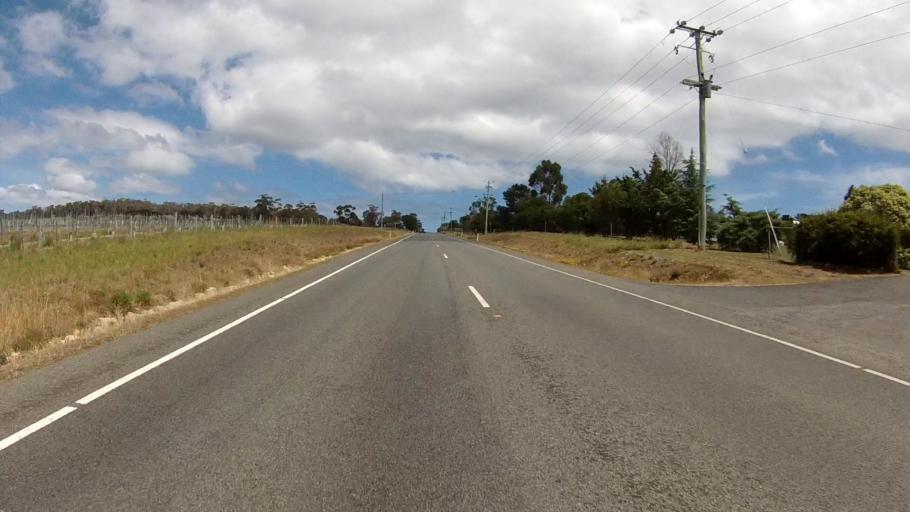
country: AU
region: Tasmania
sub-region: Sorell
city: Sorell
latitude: -42.8132
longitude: 147.6256
